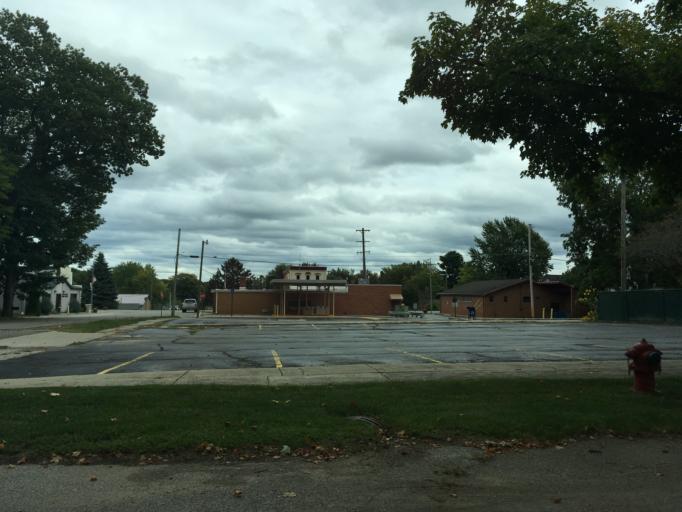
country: US
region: Michigan
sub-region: Lapeer County
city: Barnes Lake-Millers Lake
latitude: 43.3349
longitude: -83.3538
